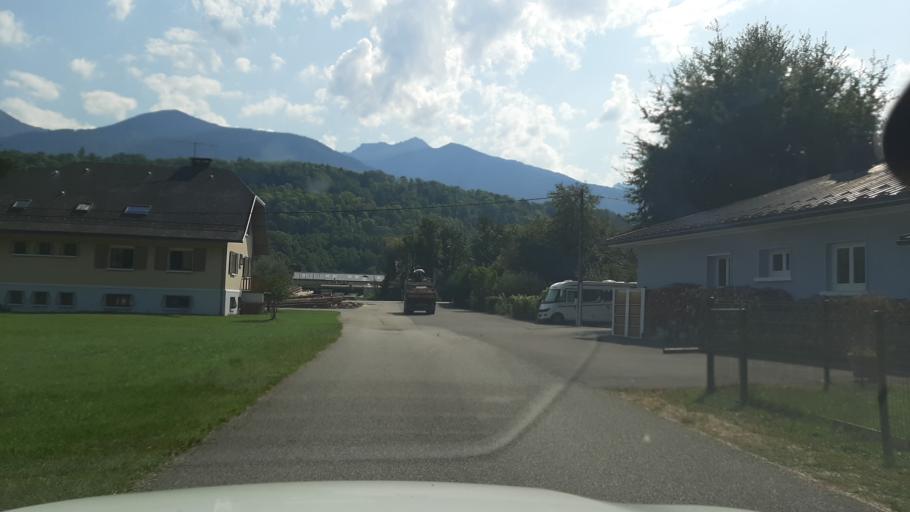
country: FR
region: Rhone-Alpes
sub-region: Departement de la Savoie
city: La Rochette
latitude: 45.4680
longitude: 6.1203
